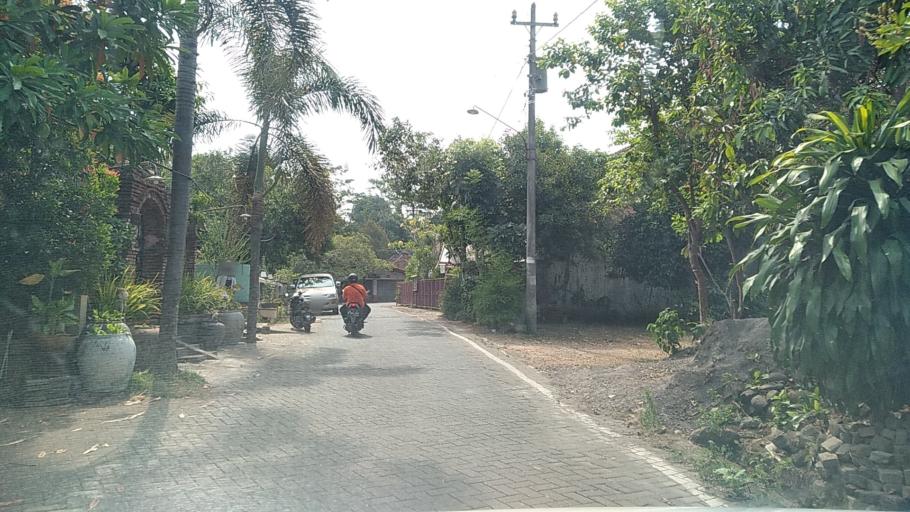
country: ID
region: Central Java
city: Ungaran
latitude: -7.0609
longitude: 110.3104
